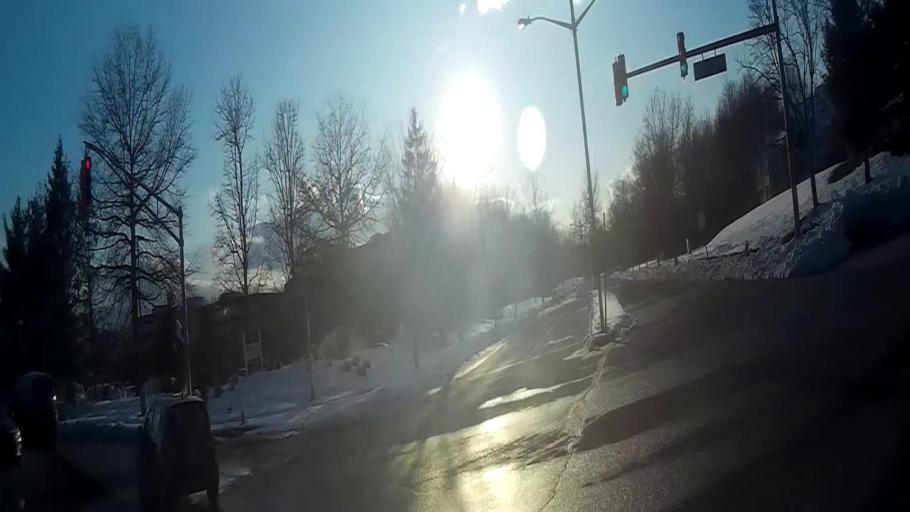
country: US
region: New Jersey
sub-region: Burlington County
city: Marlton
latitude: 39.8862
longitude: -74.9259
